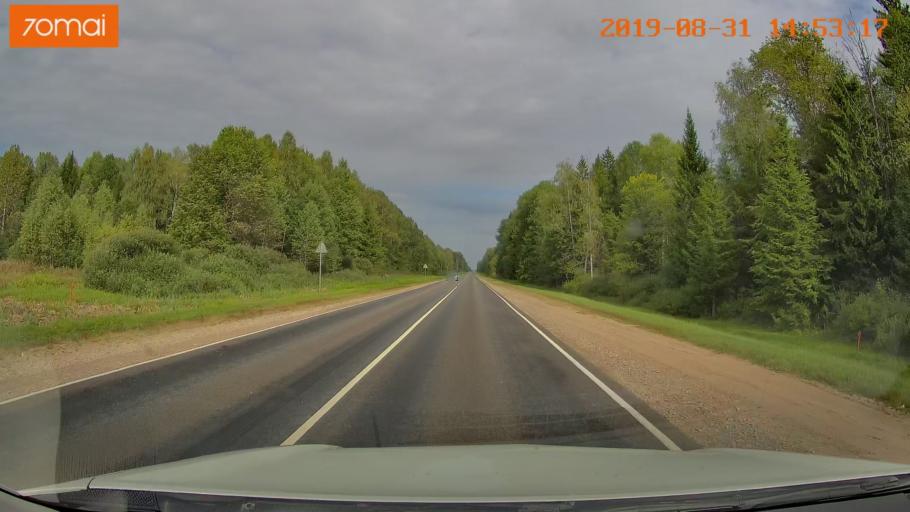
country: RU
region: Kaluga
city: Spas-Demensk
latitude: 54.2821
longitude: 33.8605
